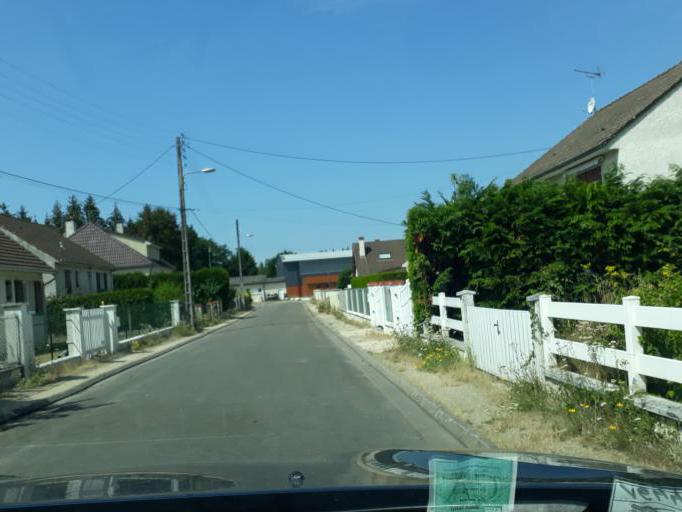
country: FR
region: Centre
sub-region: Departement du Loir-et-Cher
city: Vouzon
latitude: 47.6497
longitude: 2.0557
